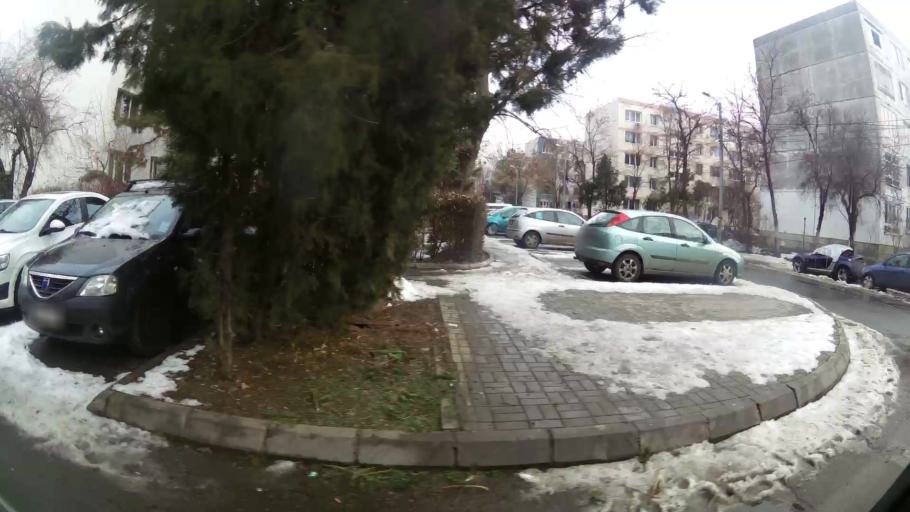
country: RO
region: Ilfov
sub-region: Comuna Popesti-Leordeni
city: Popesti-Leordeni
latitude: 44.4068
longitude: 26.1724
